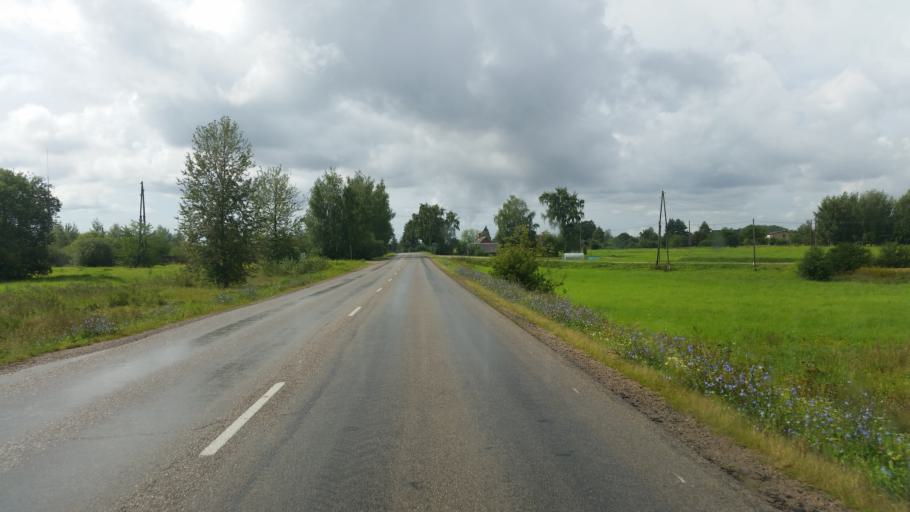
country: LV
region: Bauskas Rajons
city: Bauska
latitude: 56.4227
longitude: 24.2185
